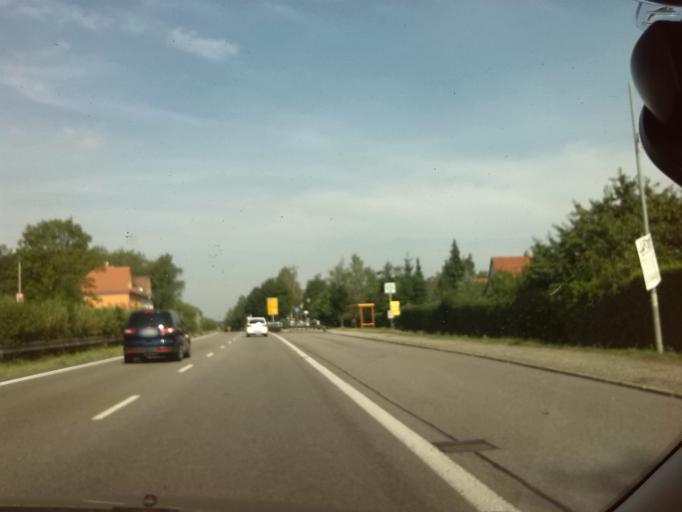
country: DE
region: Saxony
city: Espenhain
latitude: 51.1917
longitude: 12.4692
